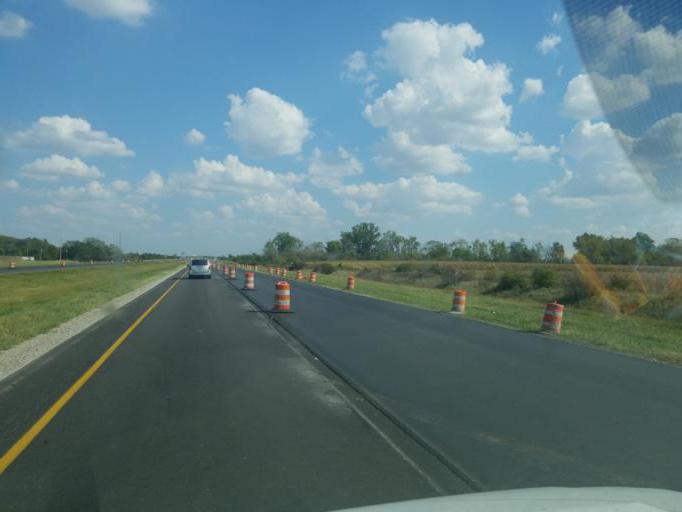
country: US
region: Ohio
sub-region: Van Wert County
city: Van Wert
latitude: 40.8696
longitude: -84.4750
